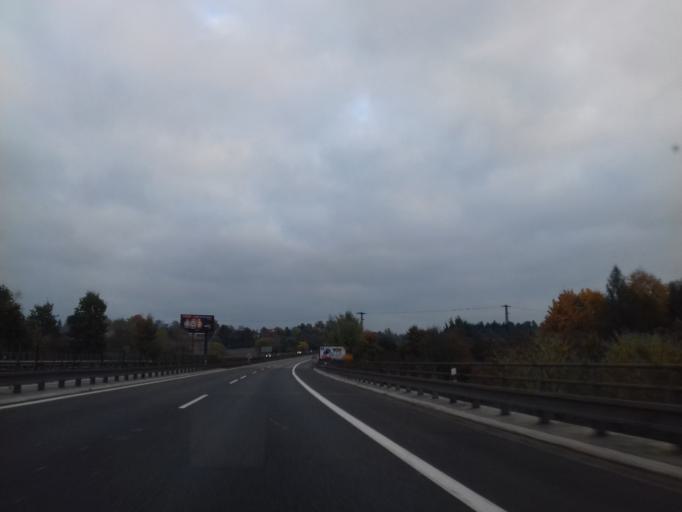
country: CZ
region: Central Bohemia
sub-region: Okres Praha-Vychod
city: Mnichovice
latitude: 49.9095
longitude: 14.7276
